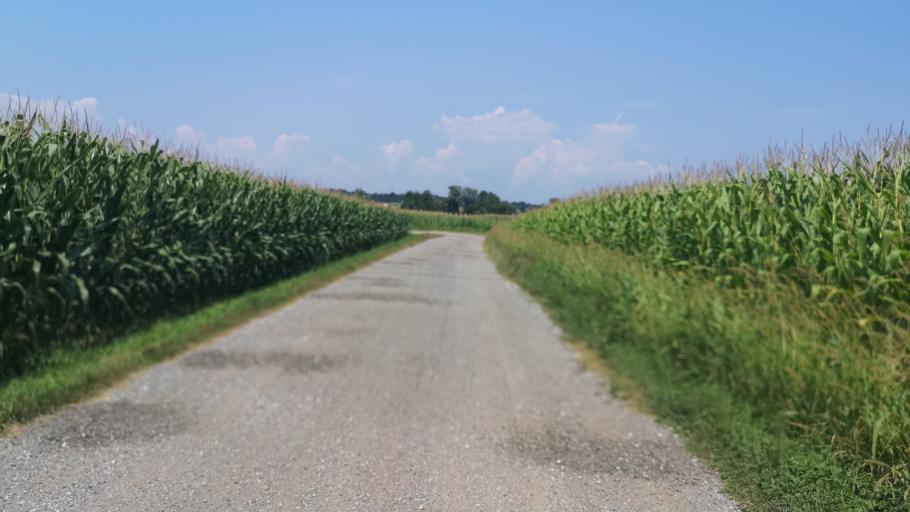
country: AT
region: Styria
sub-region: Politischer Bezirk Deutschlandsberg
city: Wettmannstatten
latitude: 46.8278
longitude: 15.3688
